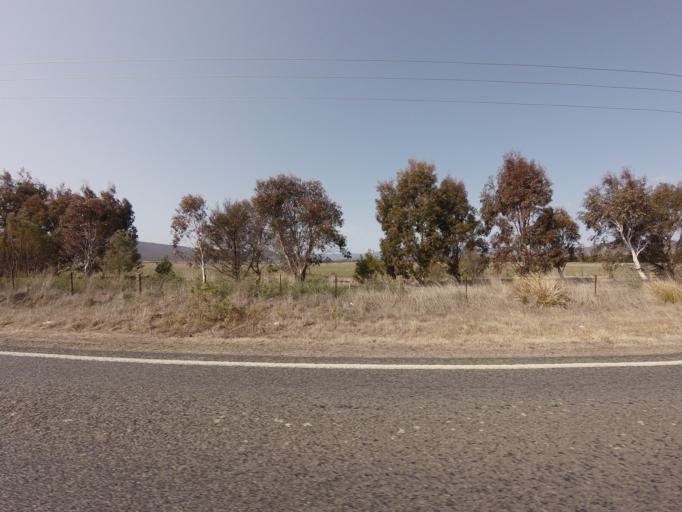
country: AU
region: Tasmania
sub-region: Northern Midlands
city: Evandale
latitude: -41.7929
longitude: 147.7101
